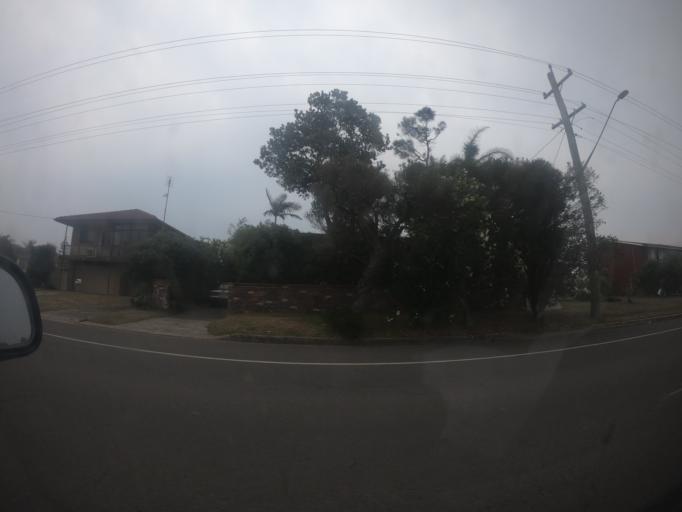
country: AU
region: New South Wales
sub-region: Shellharbour
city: Lake Illawarra
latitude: -34.5491
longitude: 150.8685
